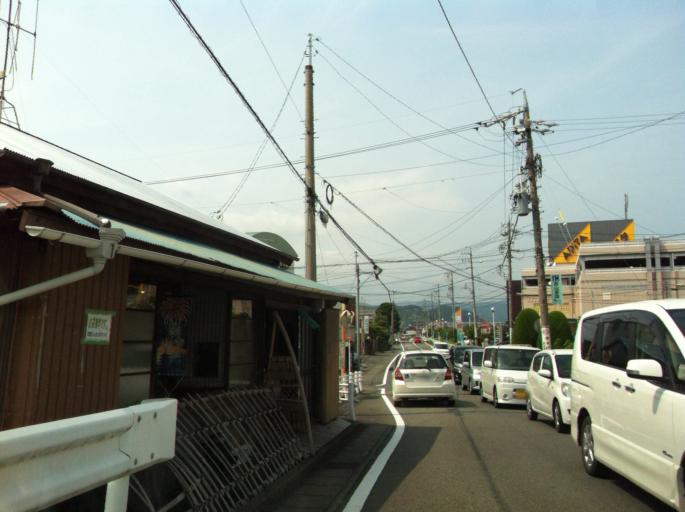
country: JP
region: Shizuoka
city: Shimada
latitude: 34.8259
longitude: 138.1843
